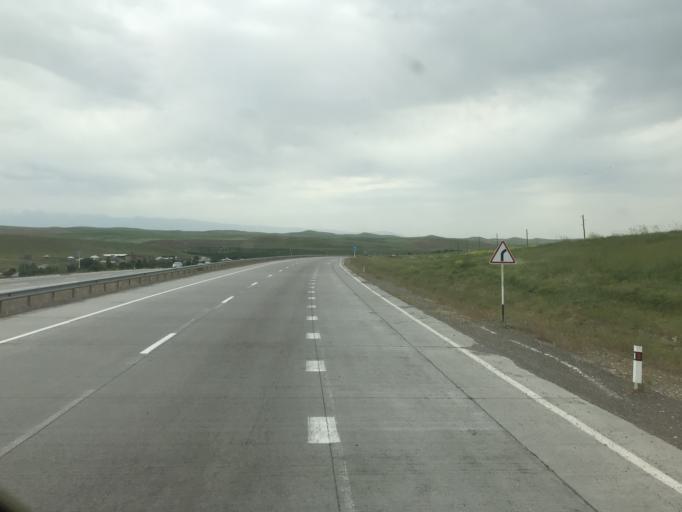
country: KZ
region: Ongtustik Qazaqstan
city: Qazyqurt
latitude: 41.9737
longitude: 69.4975
